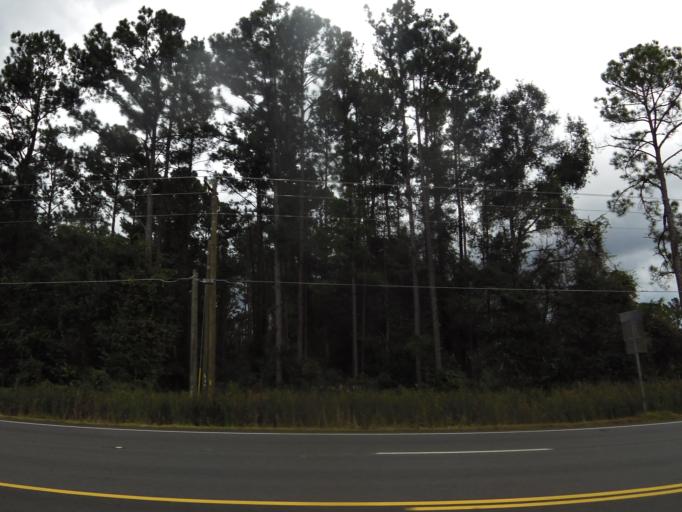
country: US
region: Georgia
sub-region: Brantley County
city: Nahunta
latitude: 31.2228
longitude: -81.8461
